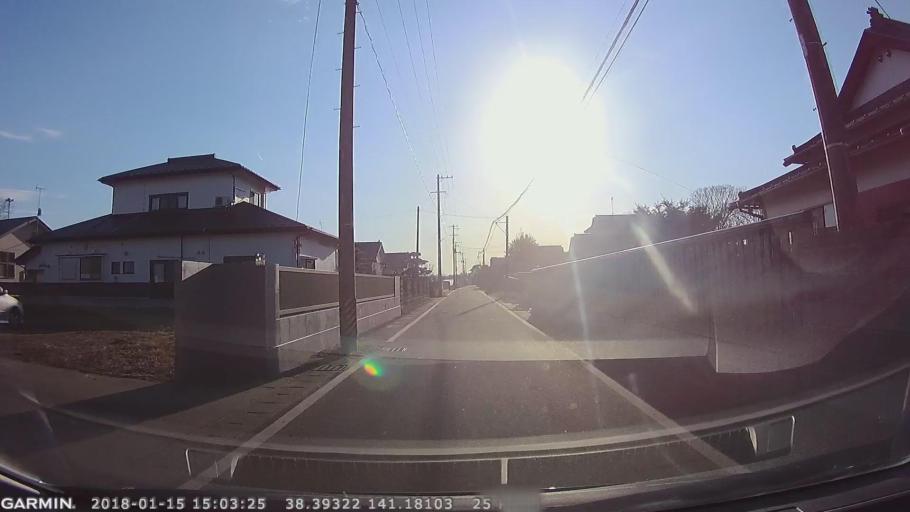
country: JP
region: Miyagi
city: Yamoto
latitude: 38.3934
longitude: 141.1811
